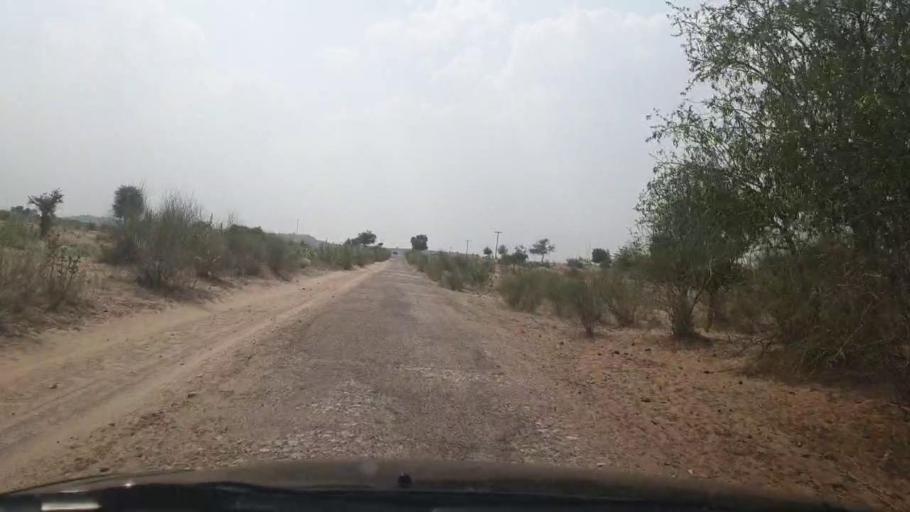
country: PK
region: Sindh
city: Islamkot
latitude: 24.9472
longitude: 70.5495
